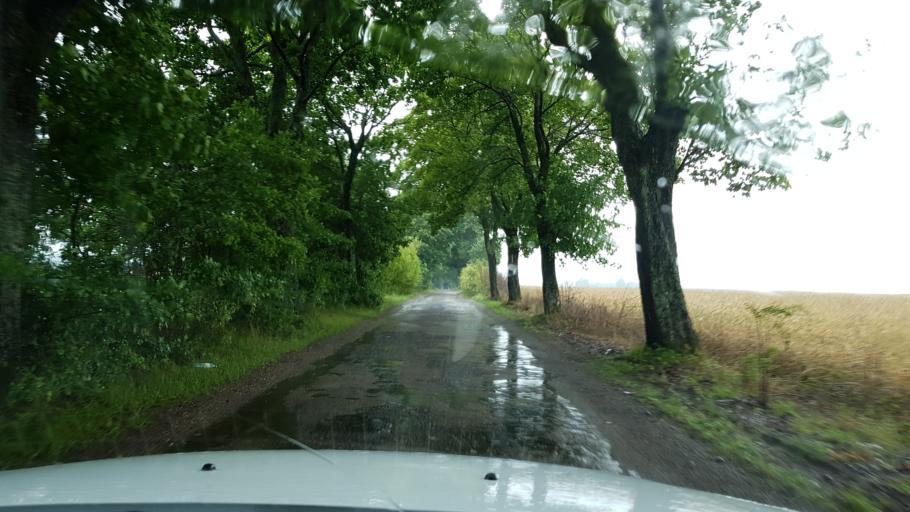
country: PL
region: West Pomeranian Voivodeship
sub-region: Powiat gryficki
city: Brojce
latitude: 53.9486
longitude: 15.4281
